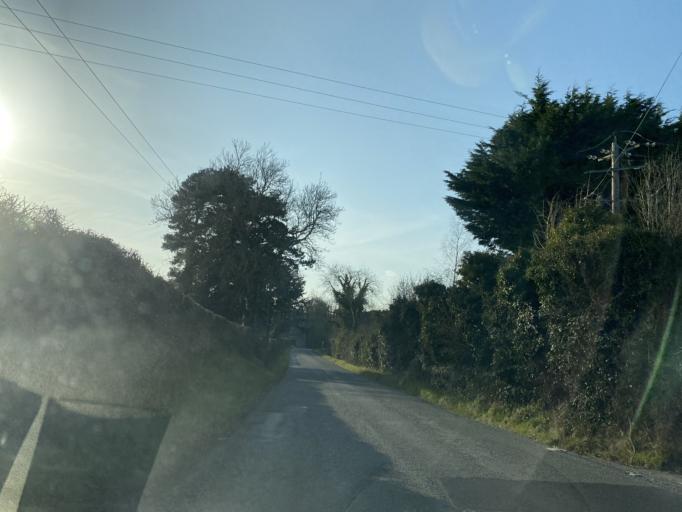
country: IE
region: Leinster
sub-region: Kildare
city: Maynooth
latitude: 53.3644
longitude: -6.5791
